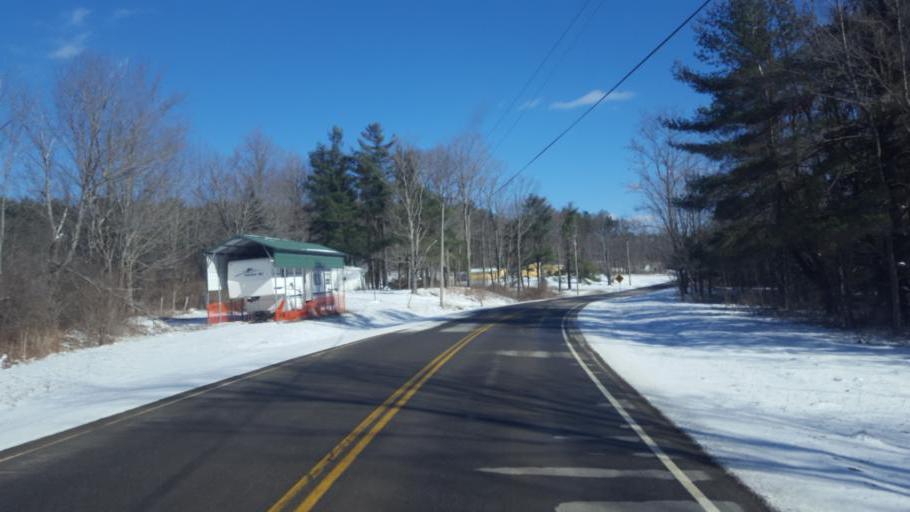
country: US
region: New York
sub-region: Allegany County
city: Belmont
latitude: 42.1731
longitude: -78.0620
